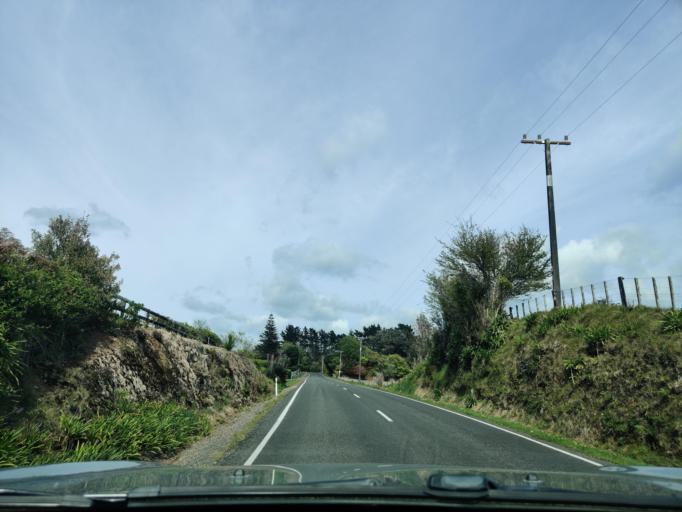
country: NZ
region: Taranaki
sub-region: New Plymouth District
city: New Plymouth
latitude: -39.1155
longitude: 174.0975
